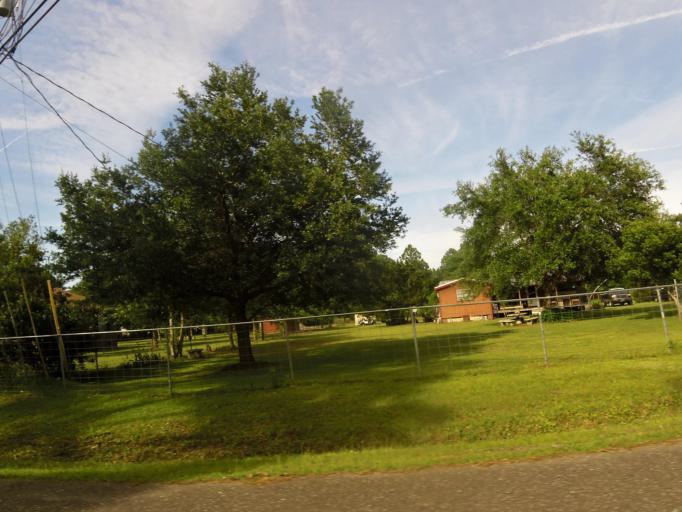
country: US
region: Florida
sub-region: Nassau County
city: Fernandina Beach
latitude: 30.5227
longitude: -81.4931
